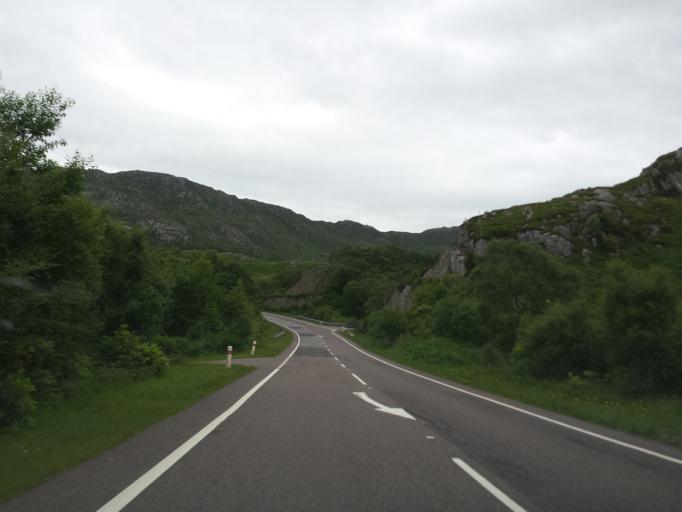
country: GB
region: Scotland
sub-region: Argyll and Bute
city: Isle Of Mull
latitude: 56.8883
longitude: -5.7080
